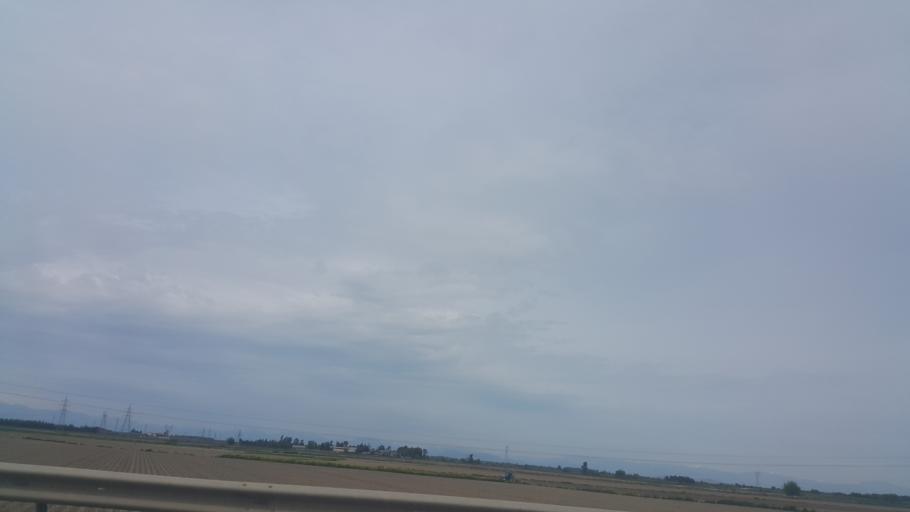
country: TR
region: Adana
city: Ceyhan
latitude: 37.0532
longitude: 35.7958
